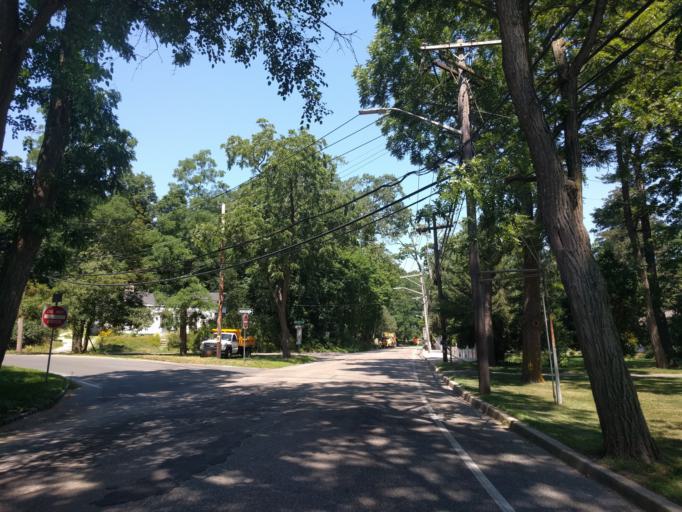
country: US
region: New York
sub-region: Suffolk County
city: Fort Salonga
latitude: 40.8990
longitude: -73.2964
